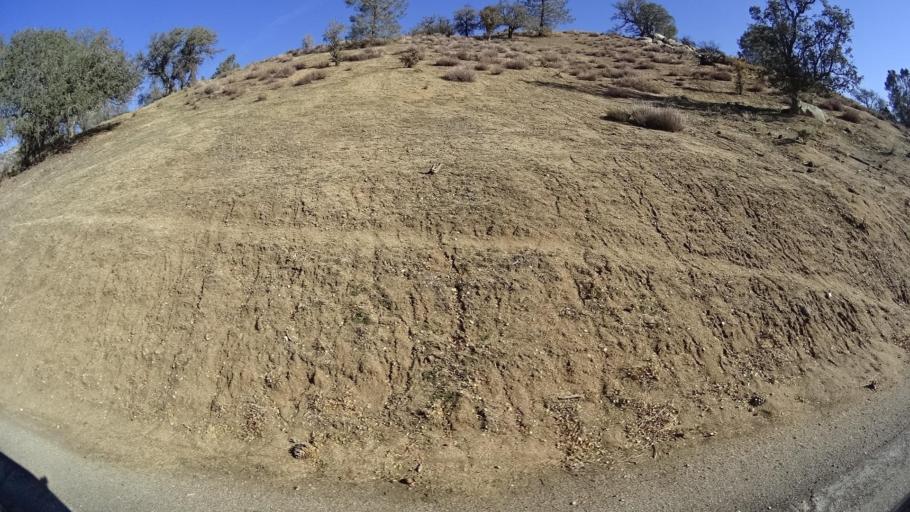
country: US
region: California
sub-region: Kern County
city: Bodfish
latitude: 35.3957
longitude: -118.4372
